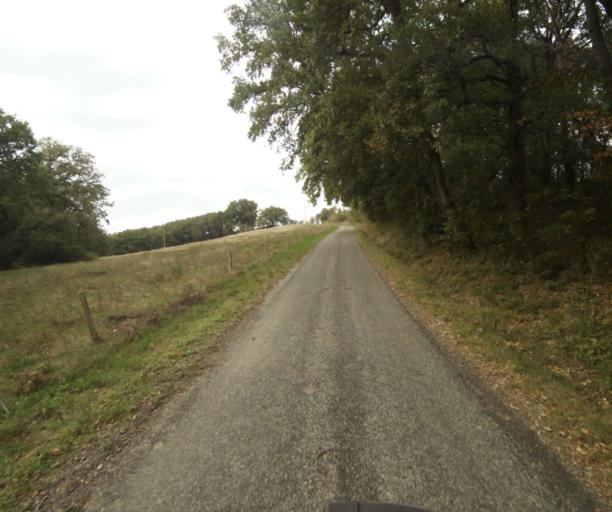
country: FR
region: Midi-Pyrenees
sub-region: Departement du Tarn-et-Garonne
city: Beaumont-de-Lomagne
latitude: 43.8292
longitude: 1.0763
